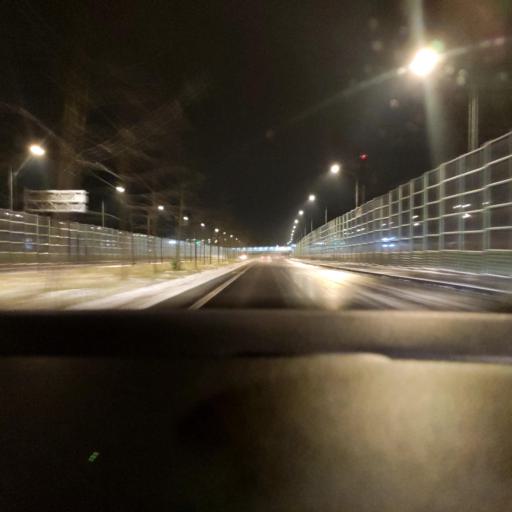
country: RU
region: Moskovskaya
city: Filimonki
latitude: 55.5711
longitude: 37.3570
